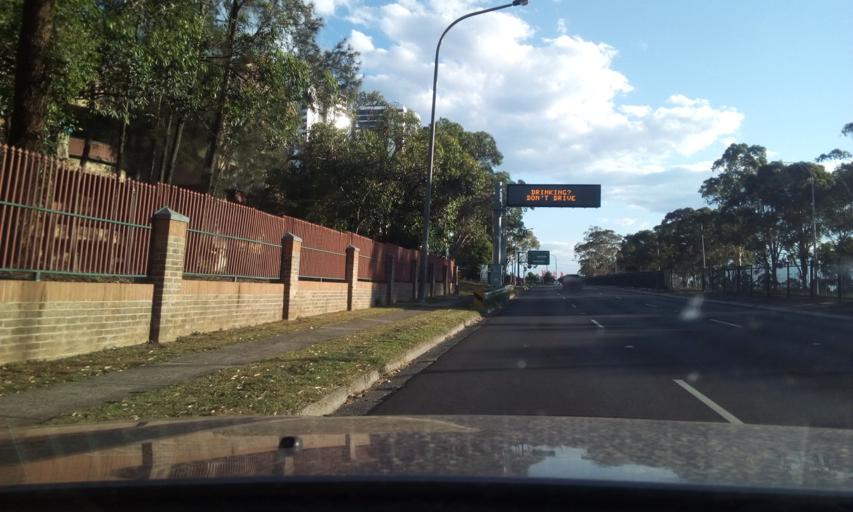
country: AU
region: New South Wales
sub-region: Fairfield
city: Liverpool
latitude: -33.9255
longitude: 150.9182
